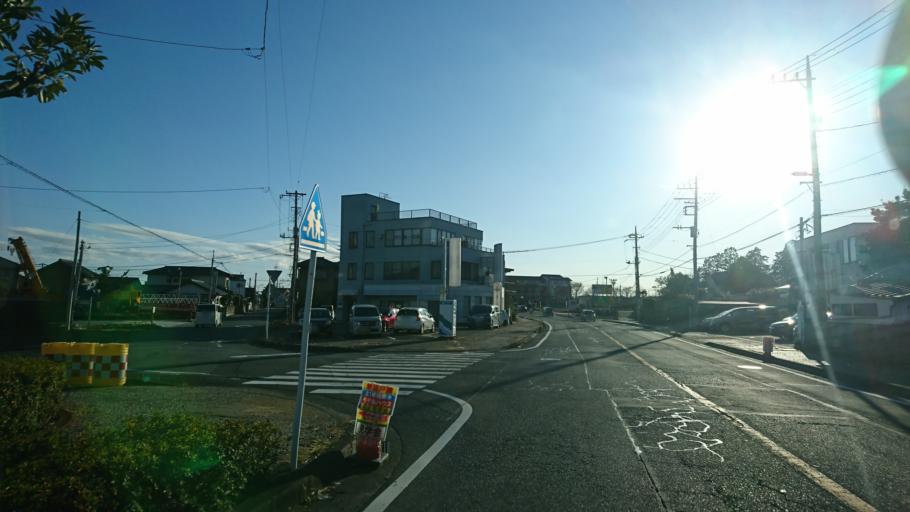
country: JP
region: Shizuoka
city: Fuji
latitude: 35.1705
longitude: 138.6544
